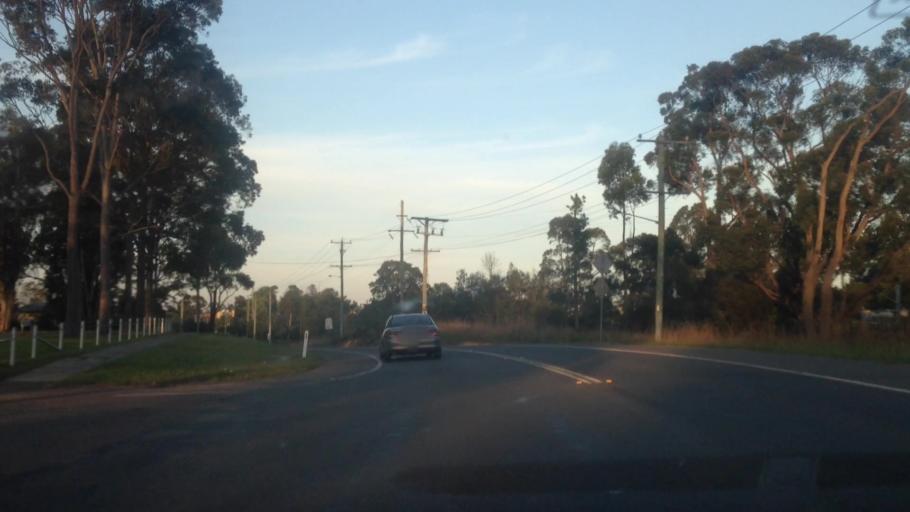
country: AU
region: New South Wales
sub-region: Lake Macquarie Shire
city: Dora Creek
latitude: -33.1111
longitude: 151.4840
